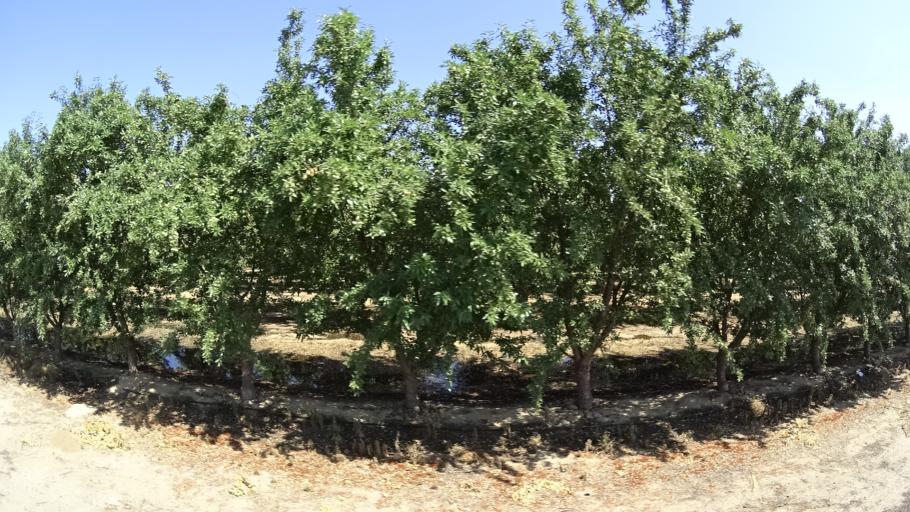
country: US
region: California
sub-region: Fresno County
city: Kingsburg
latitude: 36.4741
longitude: -119.5623
